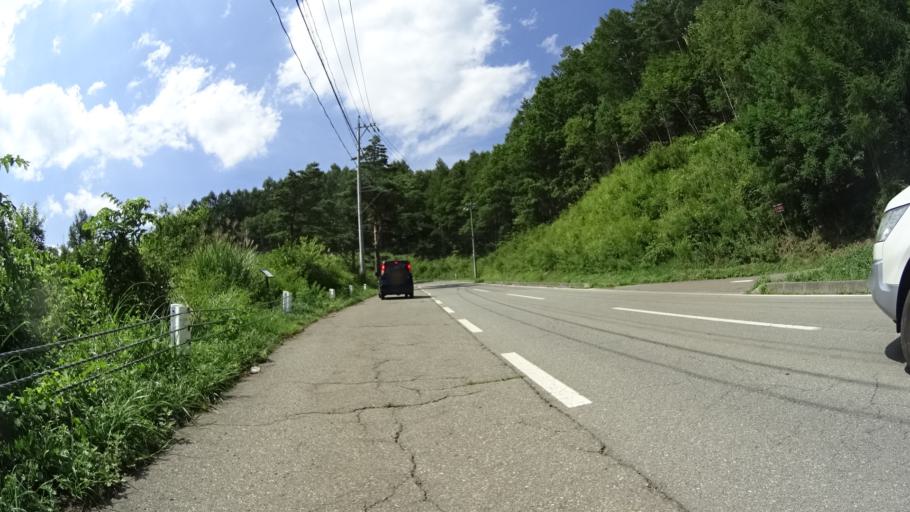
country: JP
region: Nagano
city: Saku
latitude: 36.0568
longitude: 138.4467
